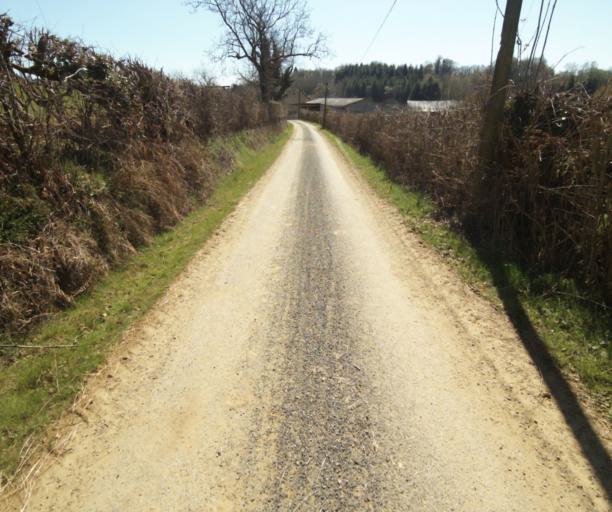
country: FR
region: Limousin
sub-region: Departement de la Correze
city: Chamboulive
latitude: 45.4625
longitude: 1.6682
